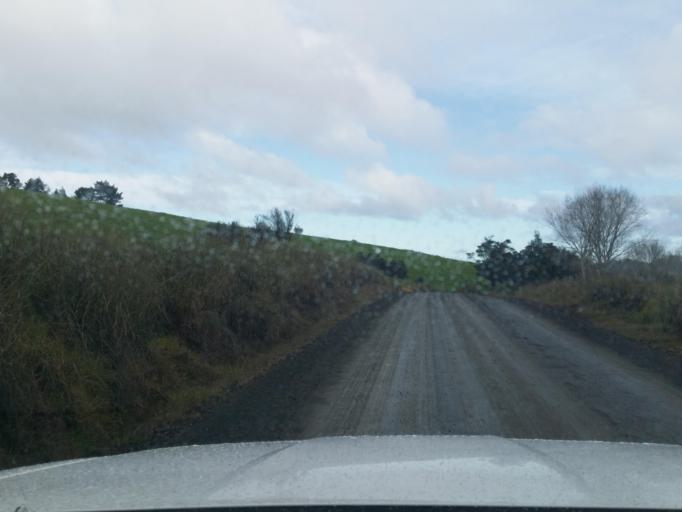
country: NZ
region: Northland
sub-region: Kaipara District
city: Dargaville
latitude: -35.8279
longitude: 173.7734
